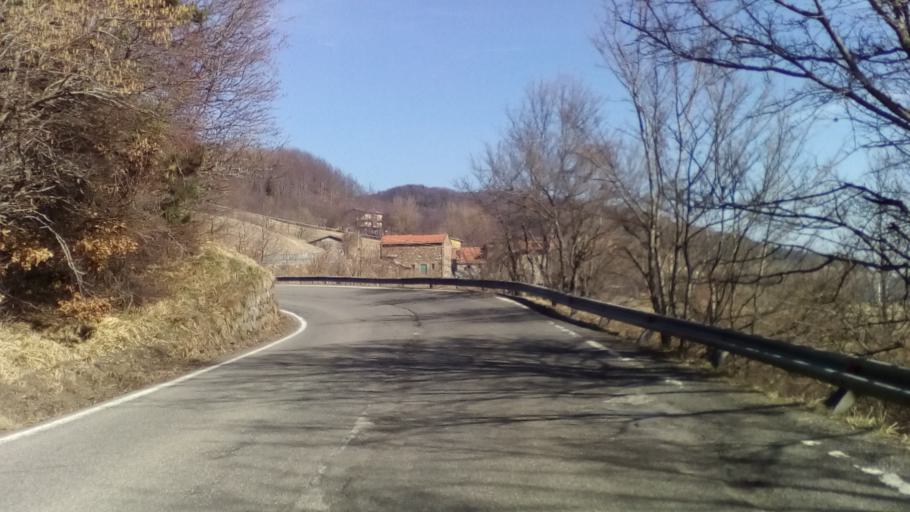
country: IT
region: Emilia-Romagna
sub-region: Provincia di Modena
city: Riolunato
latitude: 44.2630
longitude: 10.6644
